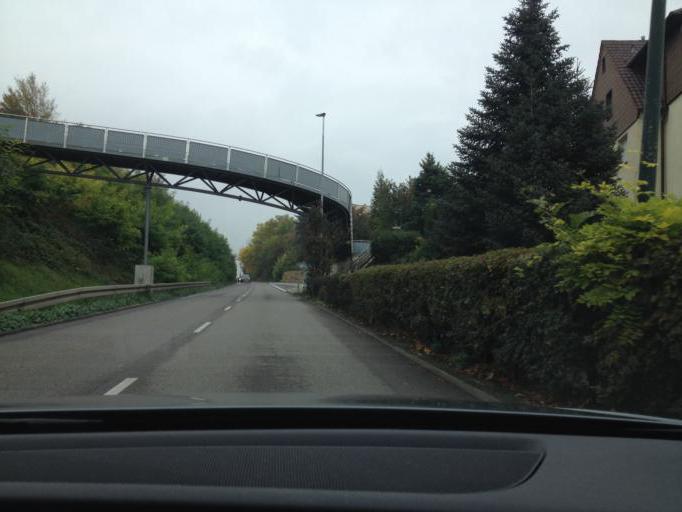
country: DE
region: Baden-Wuerttemberg
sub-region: Regierungsbezirk Stuttgart
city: Untereisesheim
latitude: 49.2124
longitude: 9.2014
